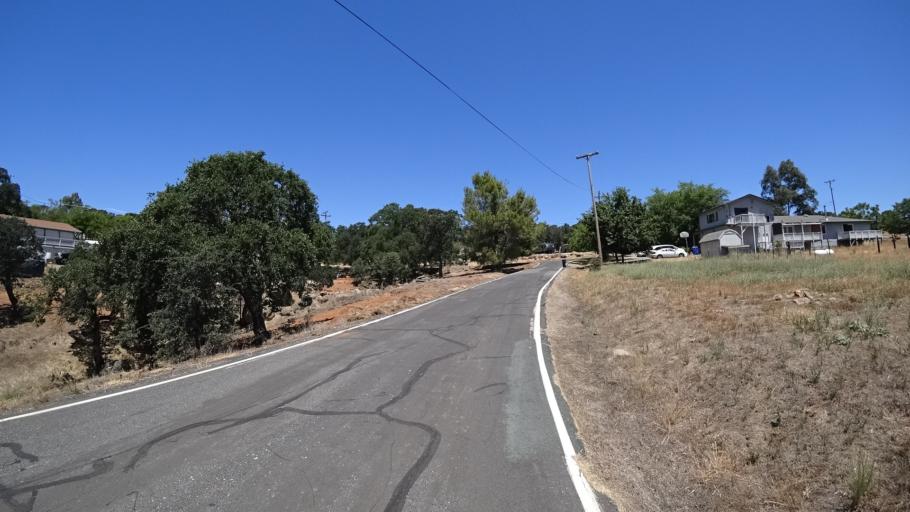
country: US
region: California
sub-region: Calaveras County
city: Rancho Calaveras
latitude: 38.1361
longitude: -120.8377
